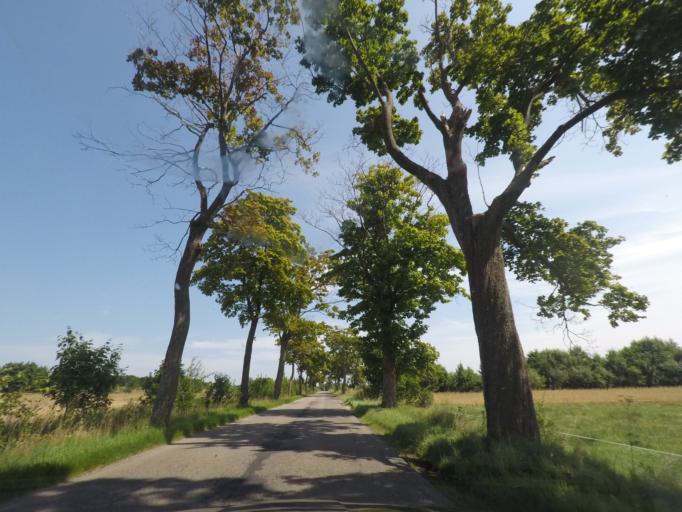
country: PL
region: West Pomeranian Voivodeship
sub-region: Powiat slawienski
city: Darlowo
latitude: 54.4631
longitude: 16.5296
